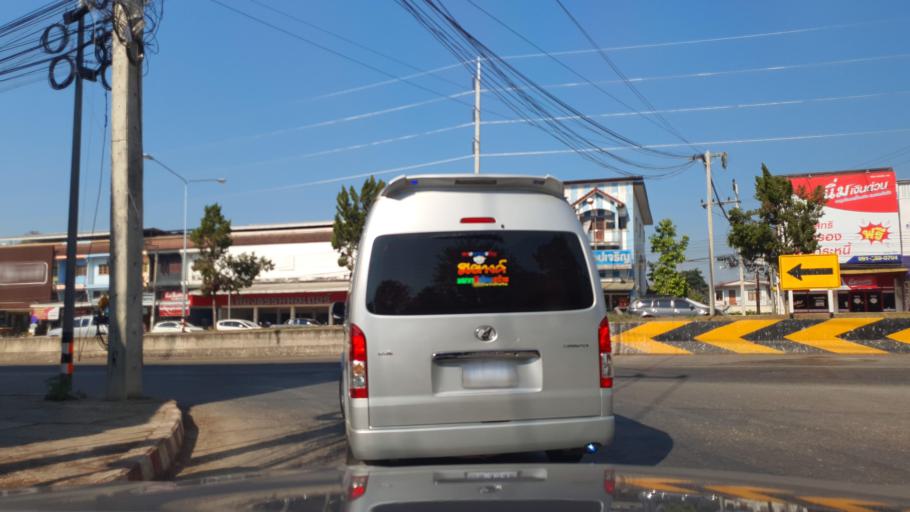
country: TH
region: Nan
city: Pua
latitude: 19.1775
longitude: 100.9153
